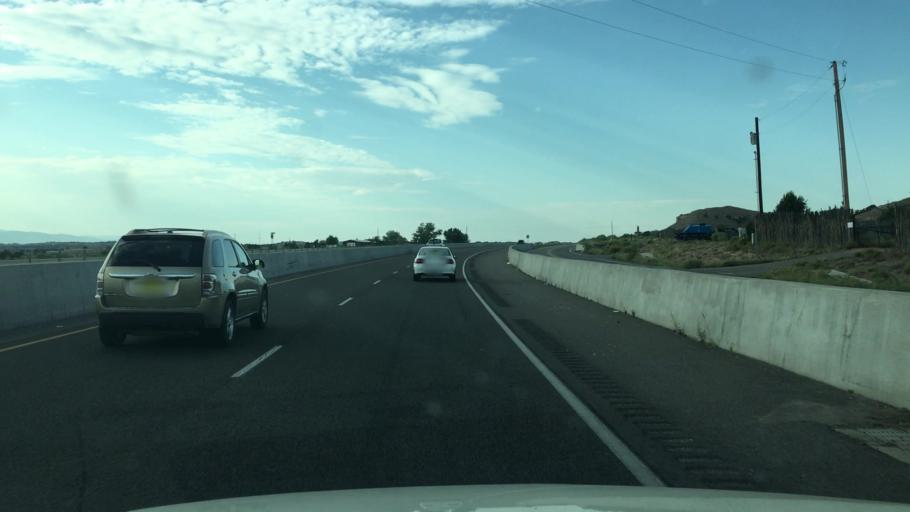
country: US
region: New Mexico
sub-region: Santa Fe County
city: El Valle de Arroyo Seco
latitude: 35.9539
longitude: -106.0214
